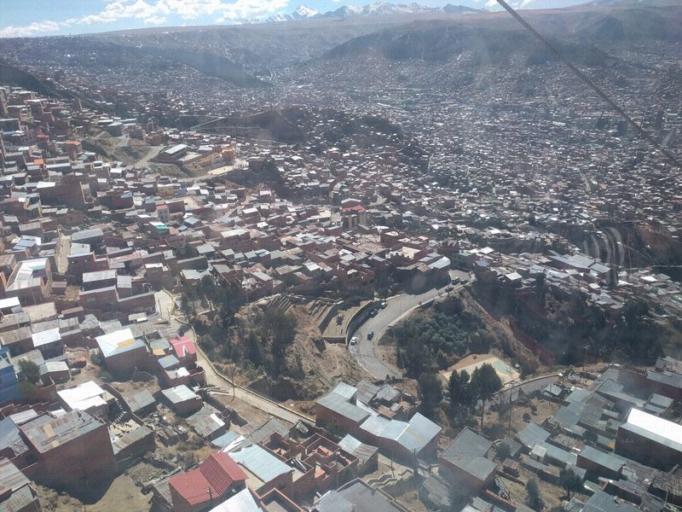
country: BO
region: La Paz
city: La Paz
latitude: -16.5177
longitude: -68.1486
